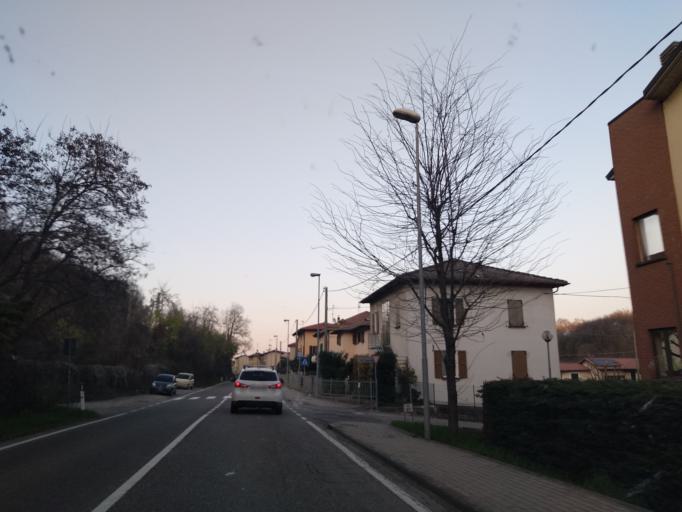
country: IT
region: Emilia-Romagna
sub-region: Provincia di Reggio Emilia
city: Vezzano sul Crostolo
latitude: 44.5931
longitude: 10.5388
